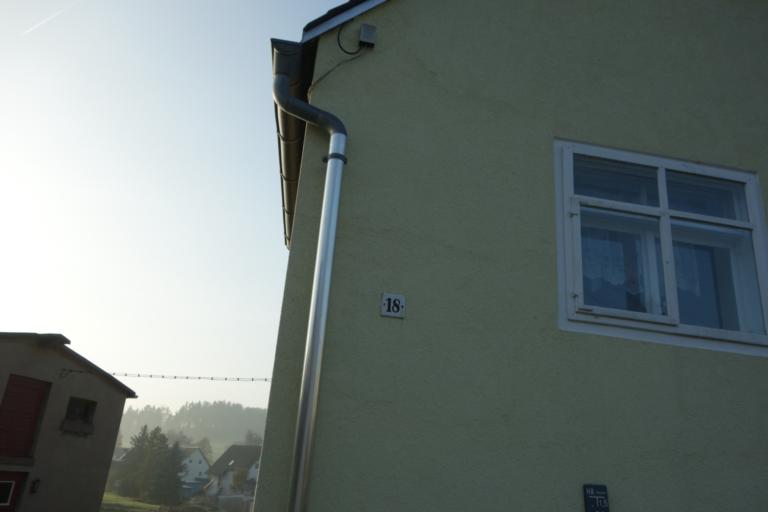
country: DE
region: Saxony
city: Lichtenberg
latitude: 50.8417
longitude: 13.4159
